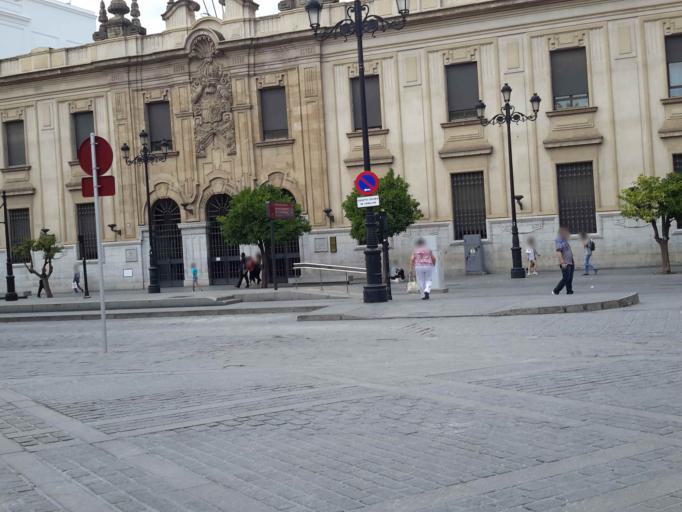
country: ES
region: Andalusia
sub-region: Provincia de Sevilla
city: Sevilla
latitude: 37.3851
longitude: -5.9936
